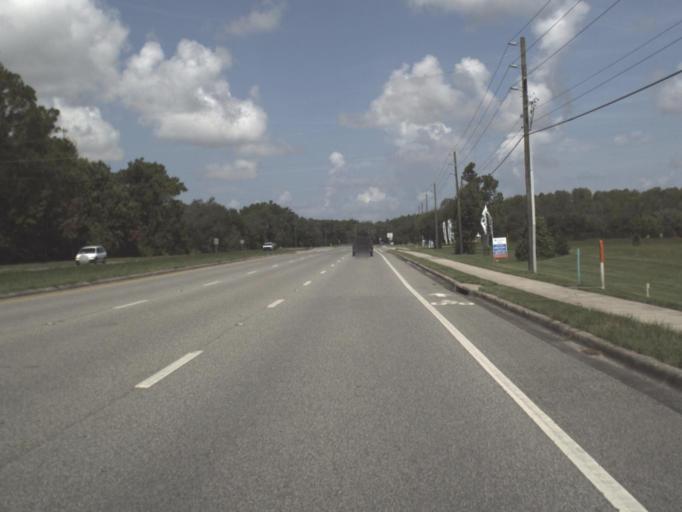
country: US
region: Florida
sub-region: Pasco County
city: Shady Hills
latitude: 28.3293
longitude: -82.5861
